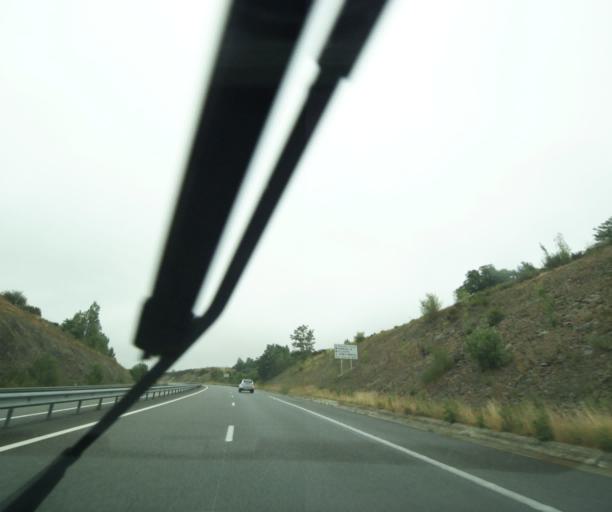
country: FR
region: Midi-Pyrenees
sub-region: Departement du Tarn
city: Carmaux
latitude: 44.0707
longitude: 2.2278
